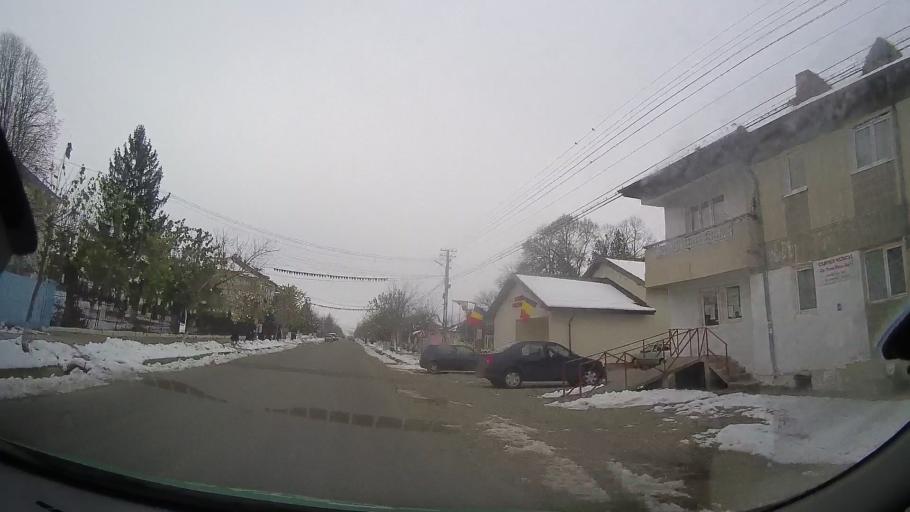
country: RO
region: Bacau
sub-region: Comuna Huruesti
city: Huruesti
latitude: 46.3020
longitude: 27.2964
